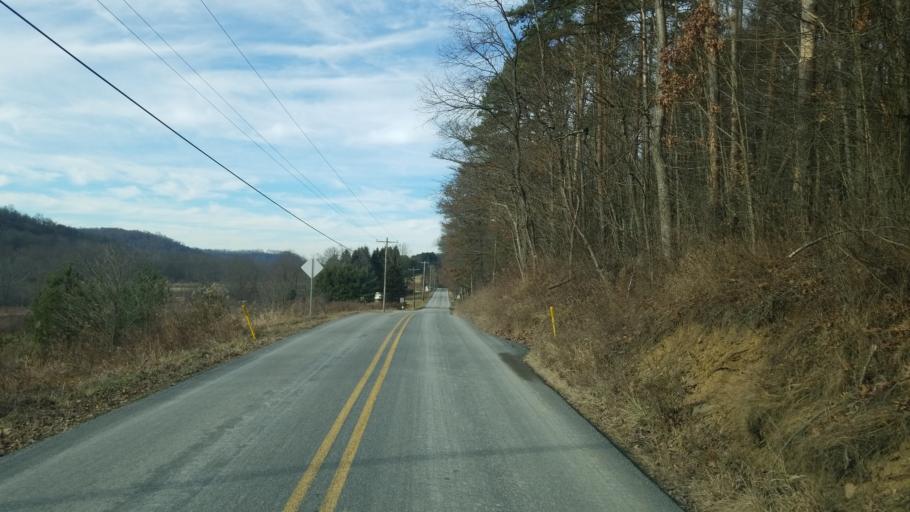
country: US
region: Pennsylvania
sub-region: Jefferson County
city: Punxsutawney
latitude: 40.8457
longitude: -79.1395
